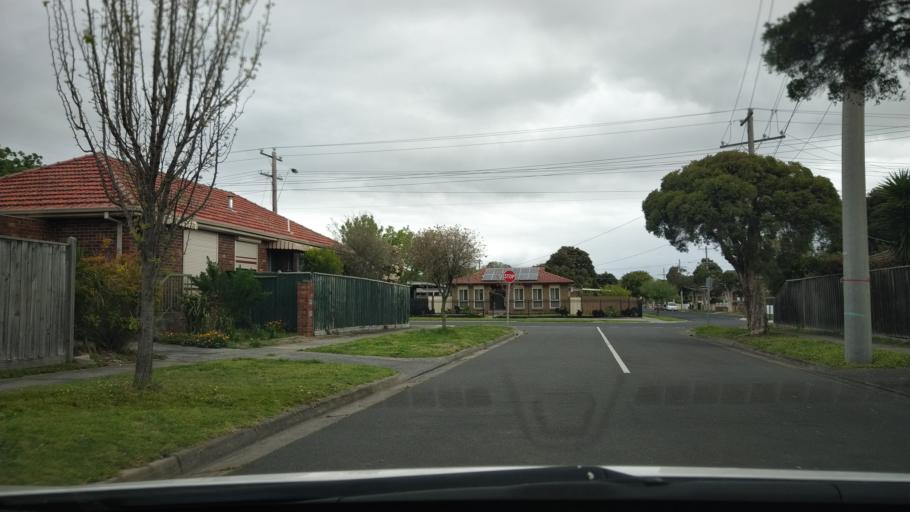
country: AU
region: Victoria
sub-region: Greater Dandenong
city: Springvale South
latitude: -37.9786
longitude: 145.1513
